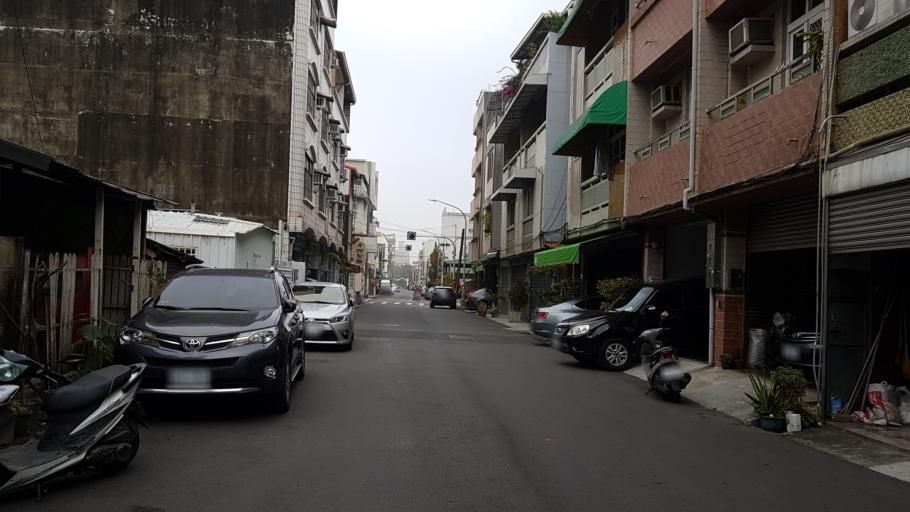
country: TW
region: Taiwan
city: Xinying
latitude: 23.3045
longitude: 120.3151
